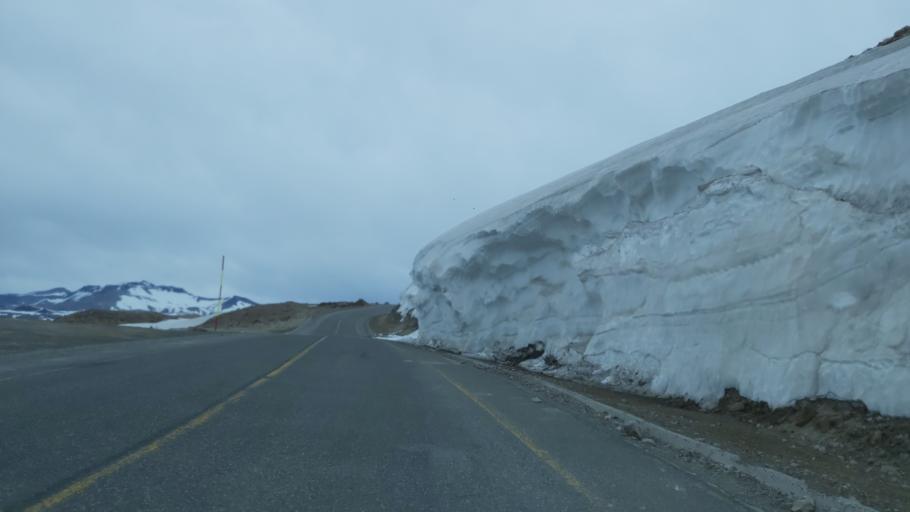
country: CL
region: Maule
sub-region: Provincia de Linares
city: Colbun
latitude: -36.0210
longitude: -70.5277
